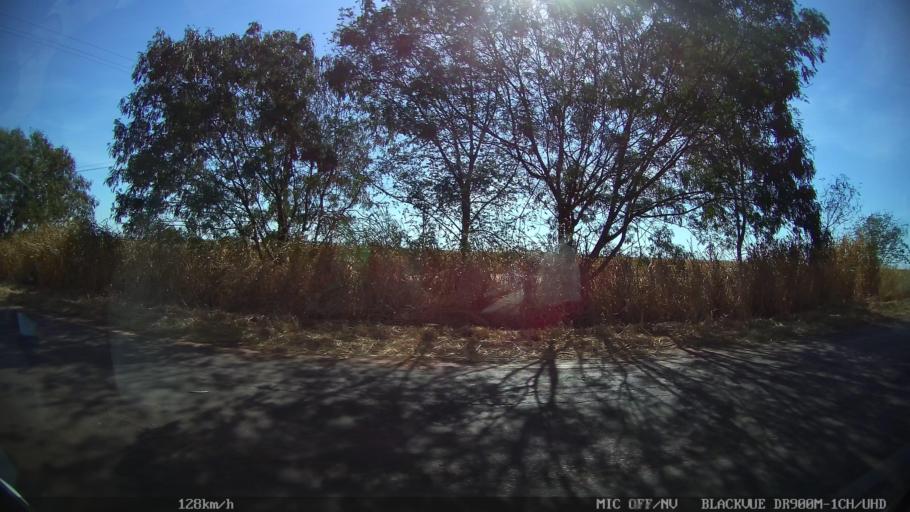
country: BR
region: Sao Paulo
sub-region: Barretos
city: Barretos
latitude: -20.4643
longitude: -48.4735
